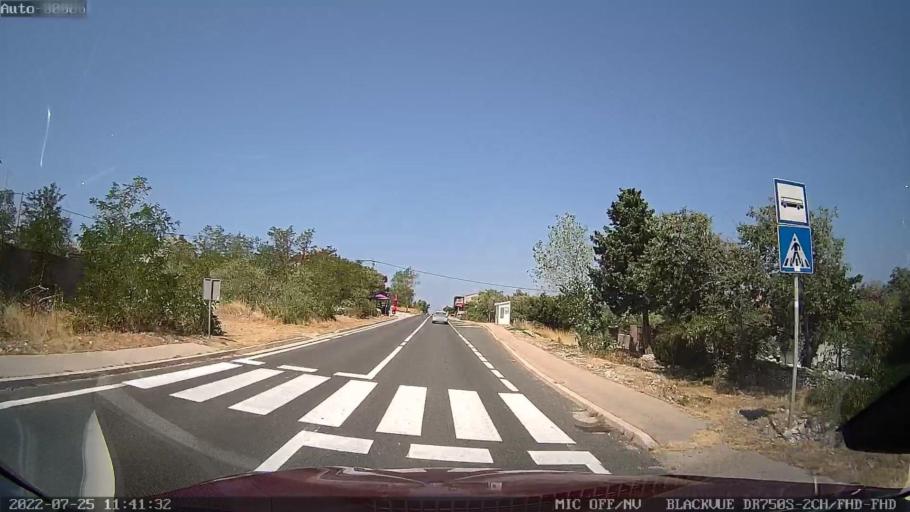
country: HR
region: Zadarska
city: Razanac
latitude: 44.2689
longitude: 15.3463
